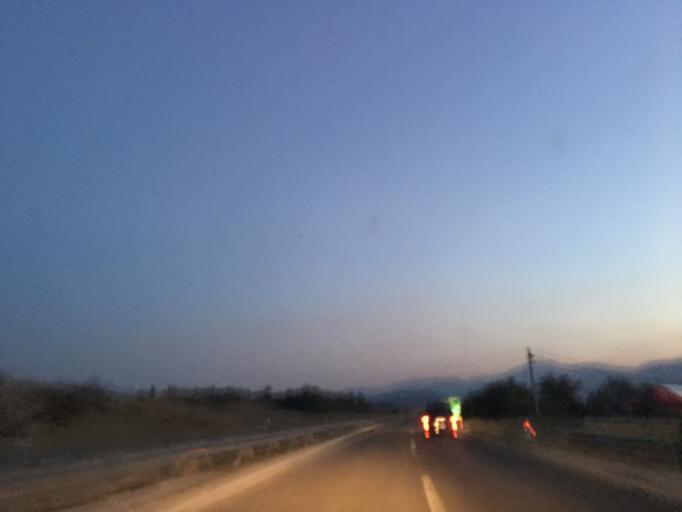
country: MK
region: Petrovec
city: Petrovec
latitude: 41.9471
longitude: 21.6306
